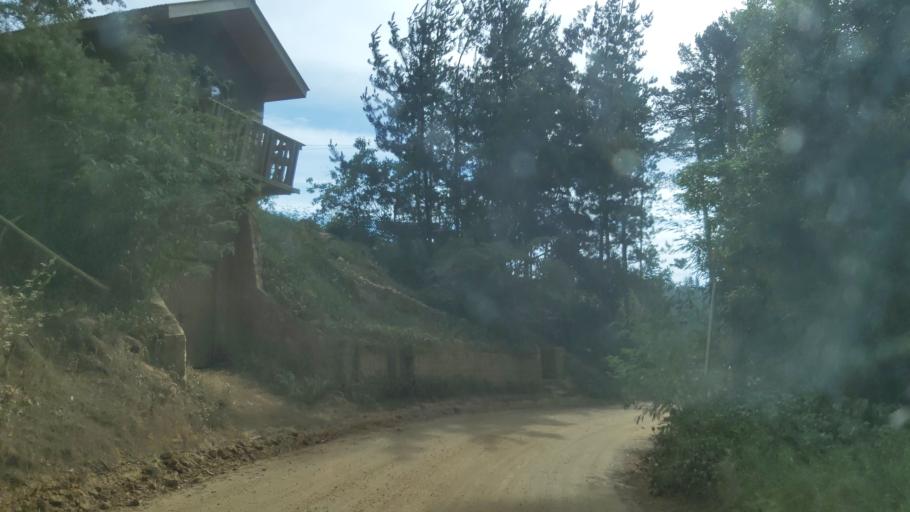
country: CL
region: Maule
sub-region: Provincia de Talca
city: Constitucion
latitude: -34.8457
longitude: -72.0396
